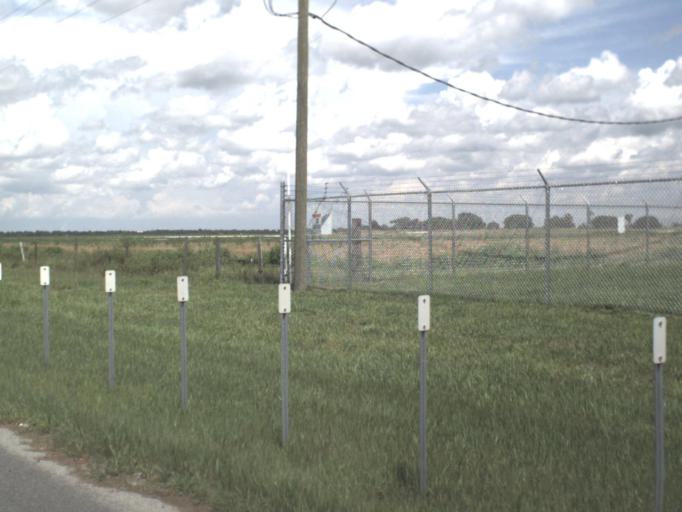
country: US
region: Florida
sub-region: Hillsborough County
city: Balm
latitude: 27.7045
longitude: -82.1470
